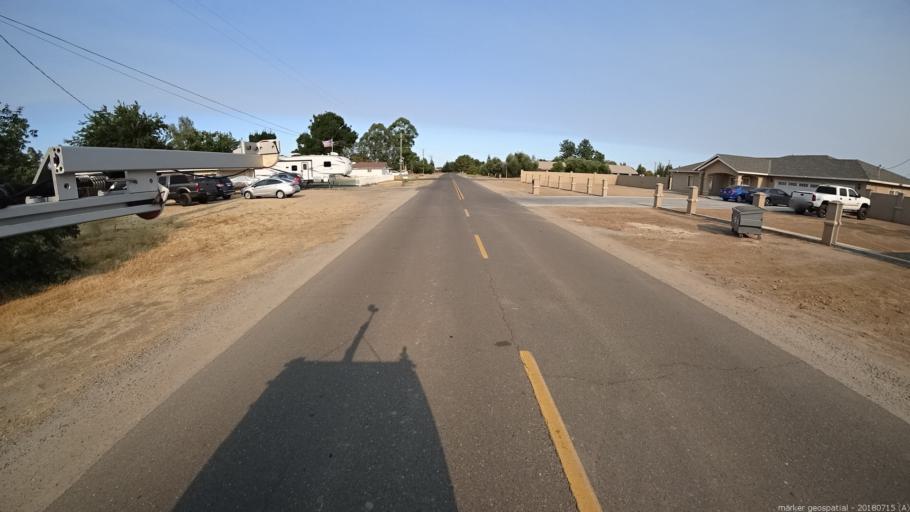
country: US
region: California
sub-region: Madera County
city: Madera Acres
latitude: 37.0125
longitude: -120.0585
